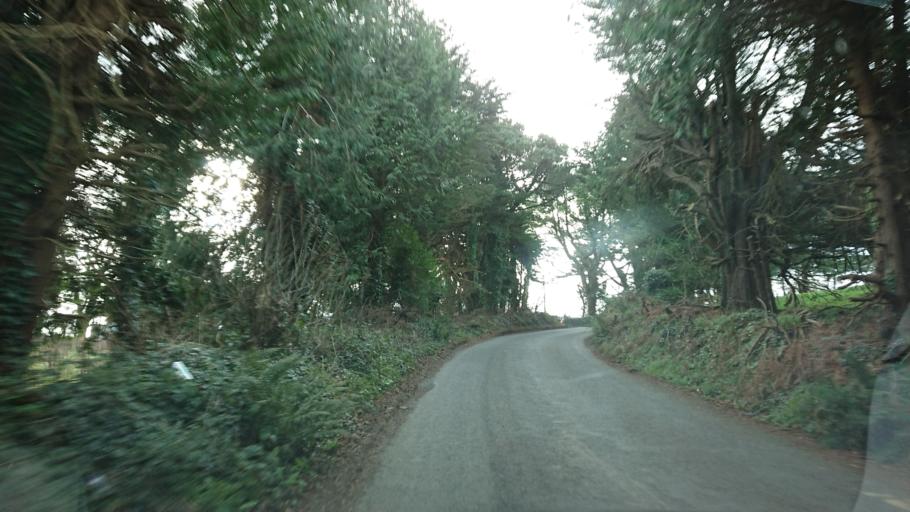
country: IE
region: Munster
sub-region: Waterford
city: Tra Mhor
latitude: 52.1758
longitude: -7.1747
